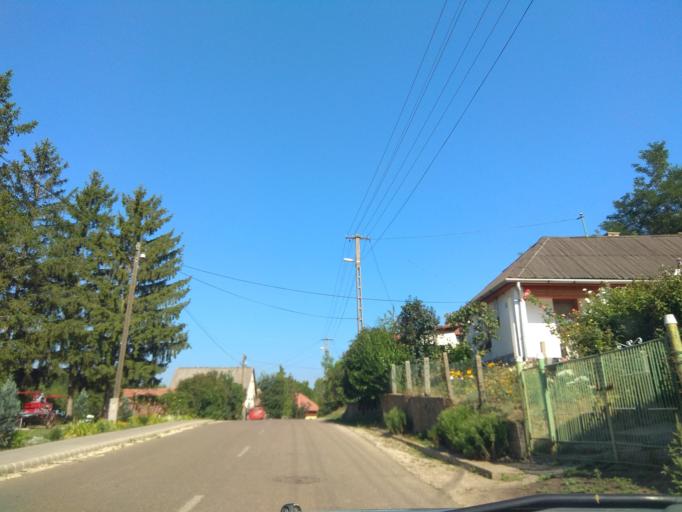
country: HU
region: Borsod-Abauj-Zemplen
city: Harsany
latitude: 47.9864
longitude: 20.7794
